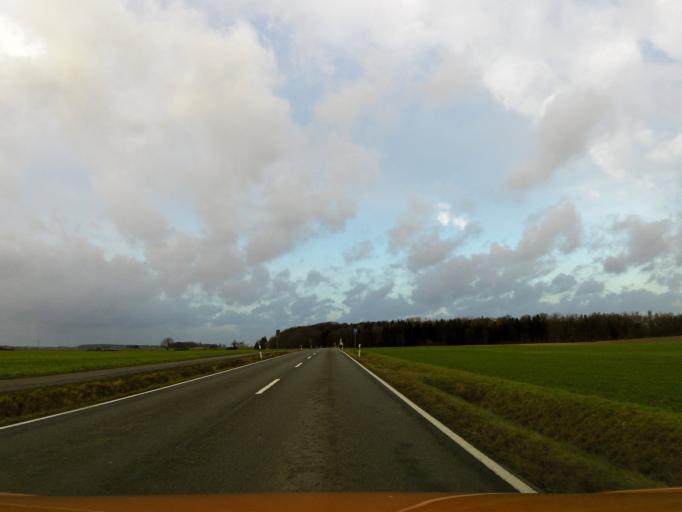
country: DE
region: Lower Saxony
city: Querenhorst
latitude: 52.3447
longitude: 10.9530
